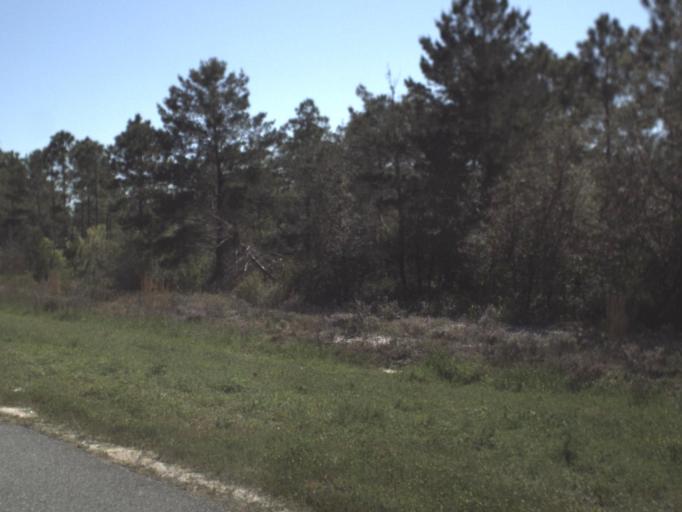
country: US
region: Florida
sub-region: Gulf County
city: Port Saint Joe
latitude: 29.8816
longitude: -85.3425
